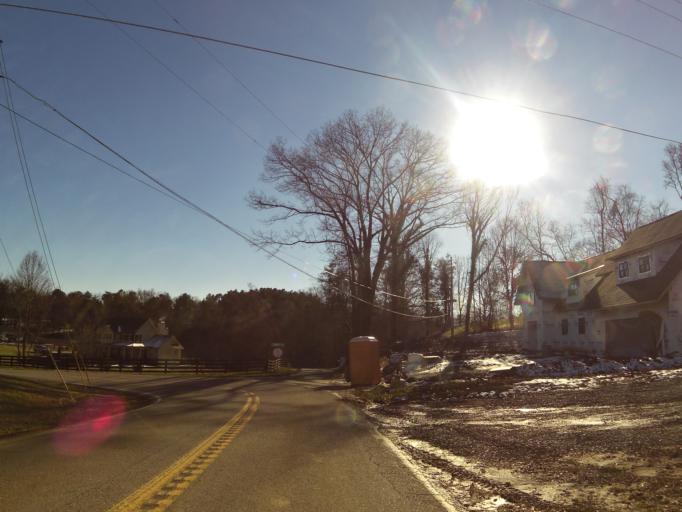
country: US
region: Tennessee
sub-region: Blount County
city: Louisville
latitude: 35.8978
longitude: -84.0032
